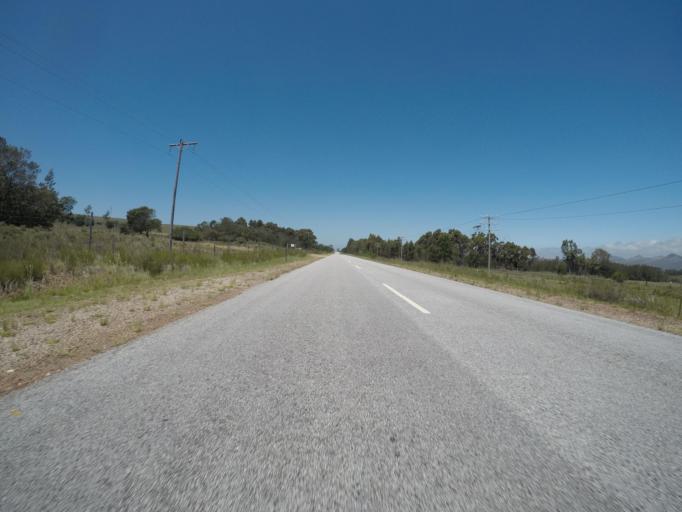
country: ZA
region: Eastern Cape
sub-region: Cacadu District Municipality
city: Kareedouw
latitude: -33.9685
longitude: 24.4546
